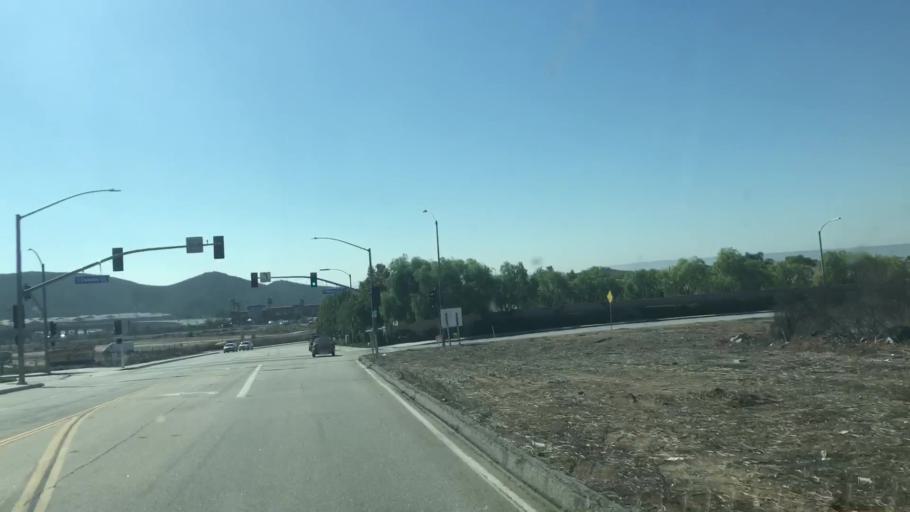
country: US
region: California
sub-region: Riverside County
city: Murrieta Hot Springs
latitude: 33.6039
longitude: -117.1758
